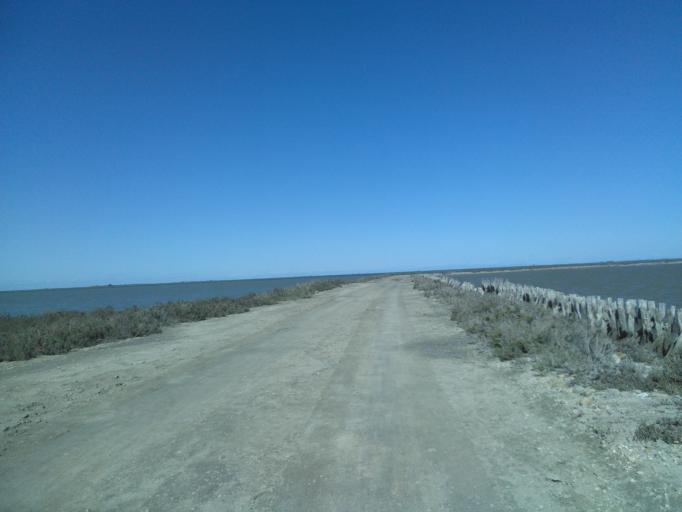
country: FR
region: Provence-Alpes-Cote d'Azur
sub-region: Departement des Bouches-du-Rhone
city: Saintes-Maries-de-la-Mer
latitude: 43.4299
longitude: 4.6175
